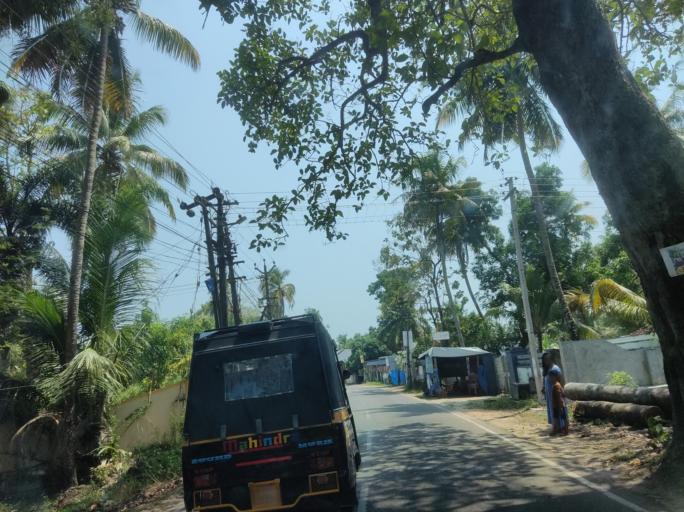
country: IN
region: Kerala
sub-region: Alappuzha
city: Kutiatodu
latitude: 9.8143
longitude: 76.2997
